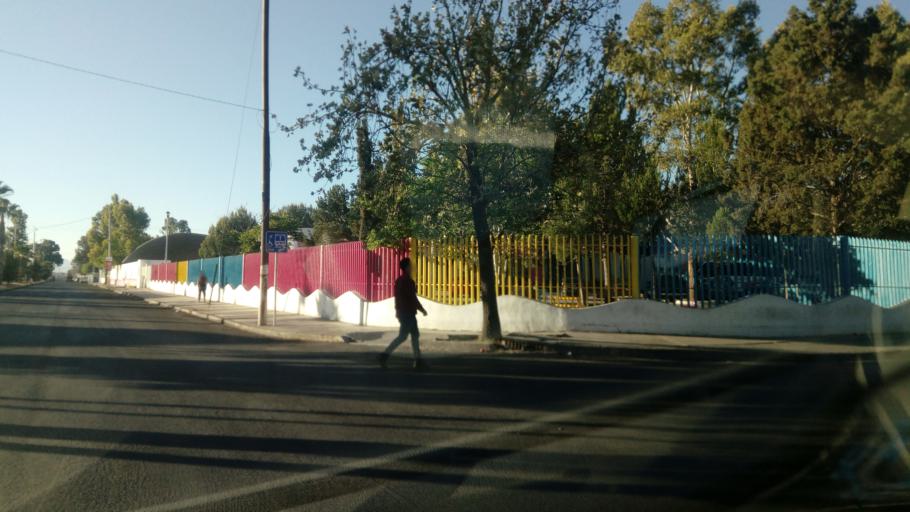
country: MX
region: Durango
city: Victoria de Durango
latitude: 24.0641
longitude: -104.5978
